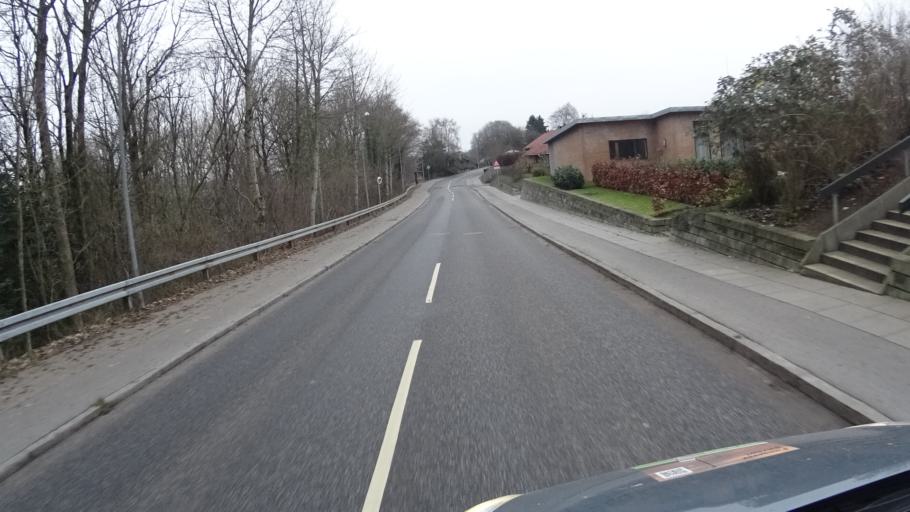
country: DK
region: South Denmark
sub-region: Vejle Kommune
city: Vejle
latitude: 55.7154
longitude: 9.6082
